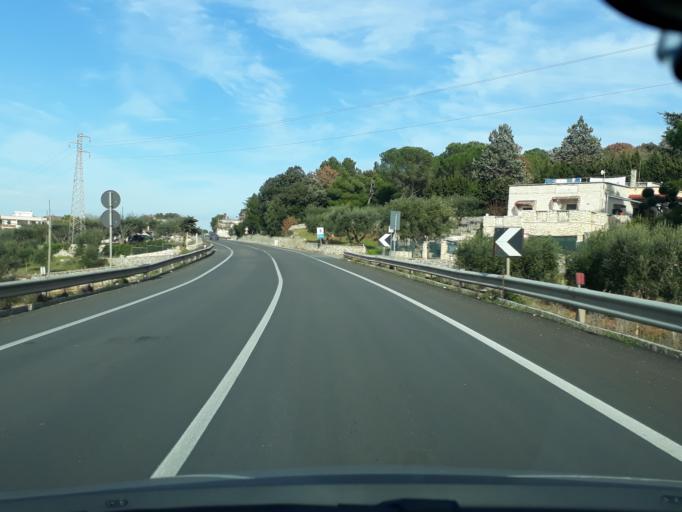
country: IT
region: Apulia
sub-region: Provincia di Bari
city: Locorotondo
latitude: 40.7802
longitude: 17.3386
